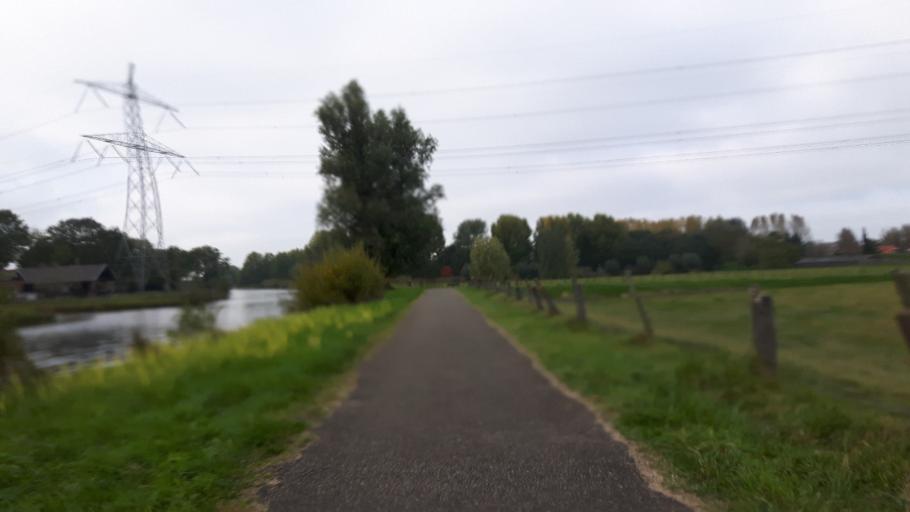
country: NL
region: South Holland
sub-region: Gemeente Vlist
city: Haastrecht
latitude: 52.0020
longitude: 4.7547
